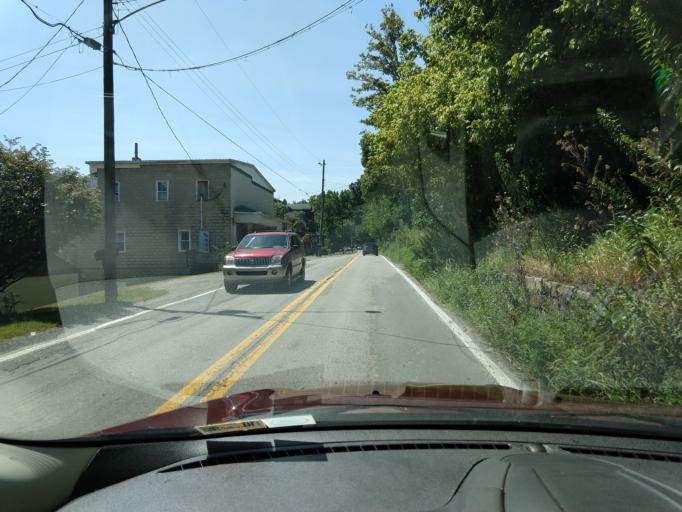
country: US
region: West Virginia
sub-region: Monongalia County
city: Morgantown
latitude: 39.6271
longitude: -79.9414
